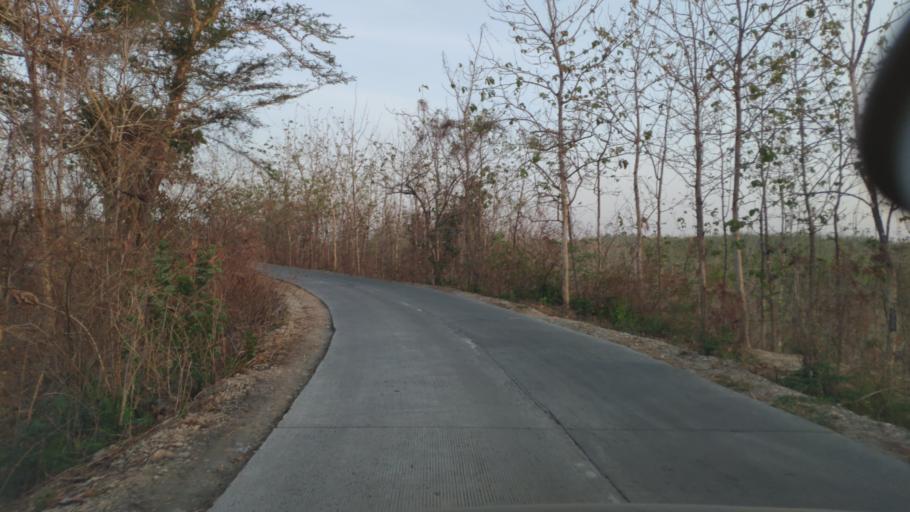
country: ID
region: Central Java
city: Semanggi
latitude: -7.0516
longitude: 111.4070
